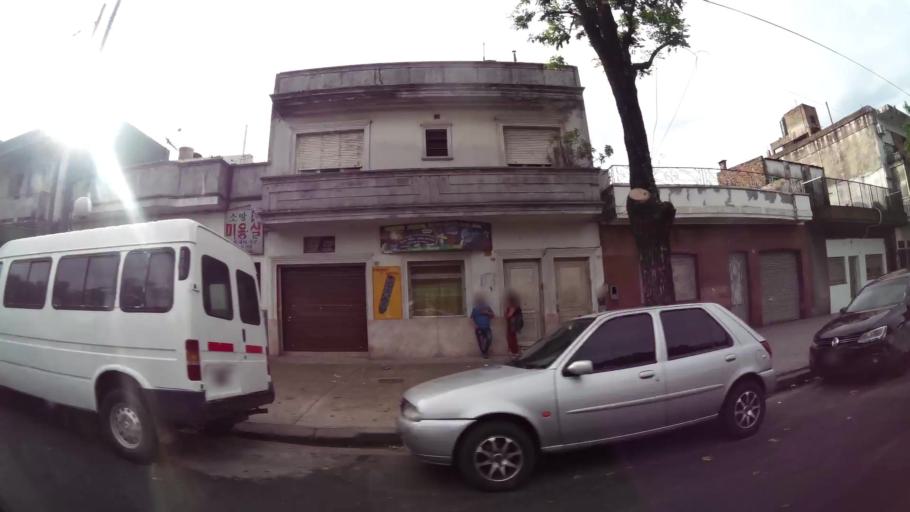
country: AR
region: Buenos Aires F.D.
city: Villa Lugano
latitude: -34.6423
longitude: -58.4437
